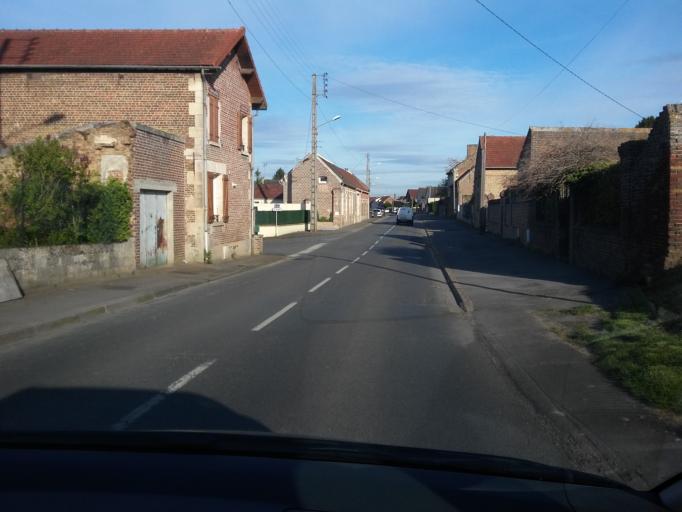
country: FR
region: Picardie
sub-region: Departement de l'Oise
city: Chevrieres
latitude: 49.3470
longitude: 2.6930
